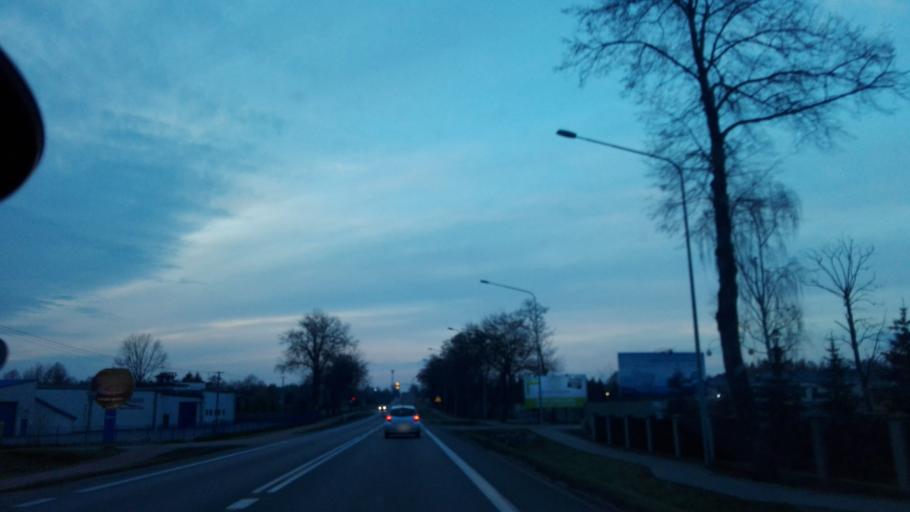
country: PL
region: Masovian Voivodeship
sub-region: Powiat siedlecki
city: Skorzec
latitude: 52.1759
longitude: 22.1927
